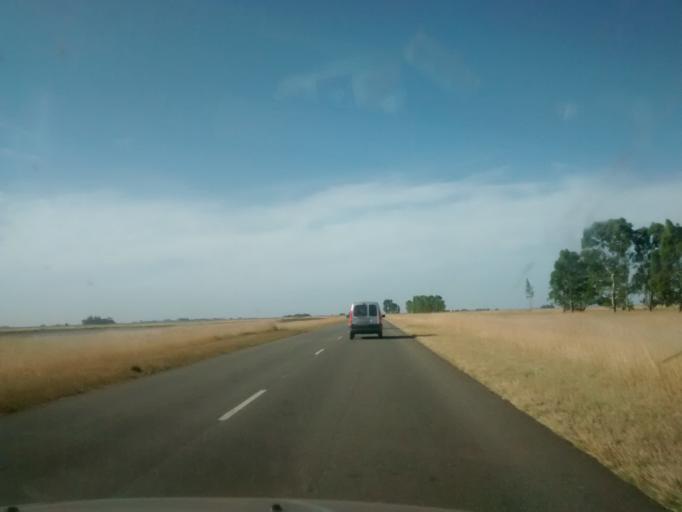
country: AR
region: Buenos Aires
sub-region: Partido de Ayacucho
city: Ayacucho
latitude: -37.3120
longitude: -58.4691
